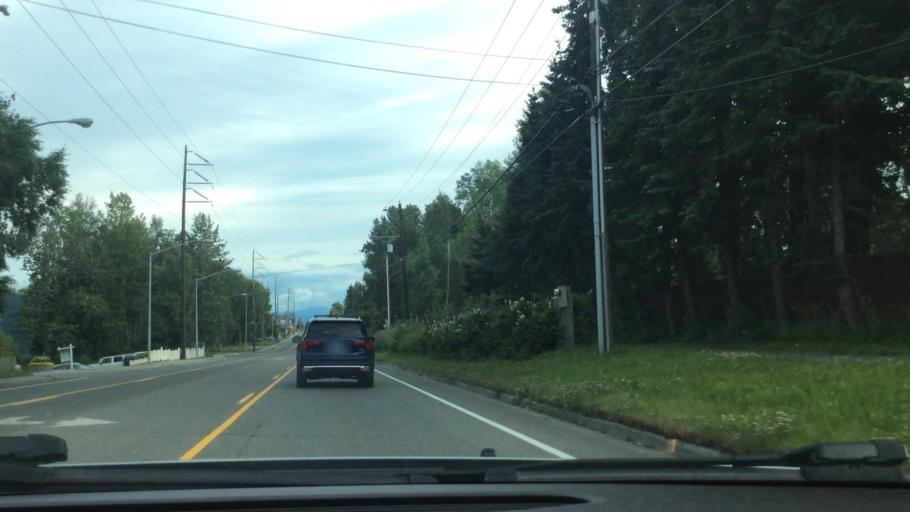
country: US
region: Alaska
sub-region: Anchorage Municipality
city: Anchorage
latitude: 61.1781
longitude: -149.8980
